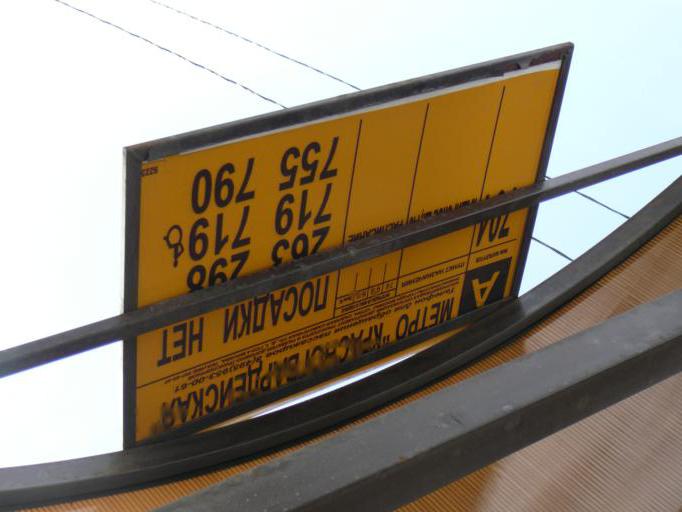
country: RU
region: Moscow
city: Orekhovo-Borisovo
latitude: 55.6128
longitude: 37.7447
